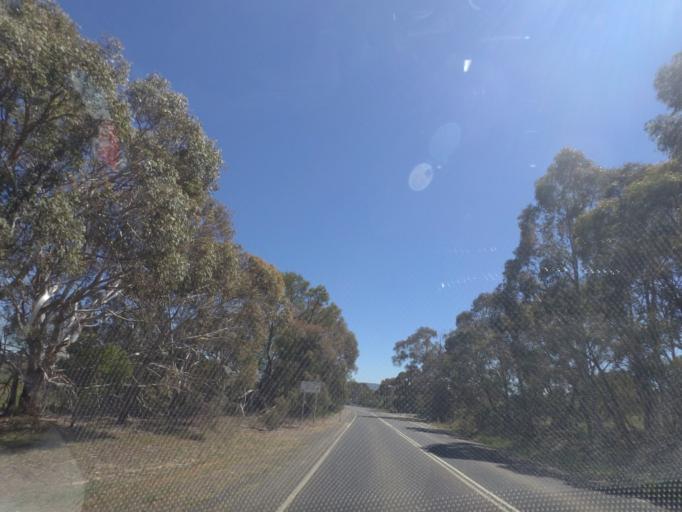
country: AU
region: Victoria
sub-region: Hume
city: Sunbury
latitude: -37.2884
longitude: 144.7882
